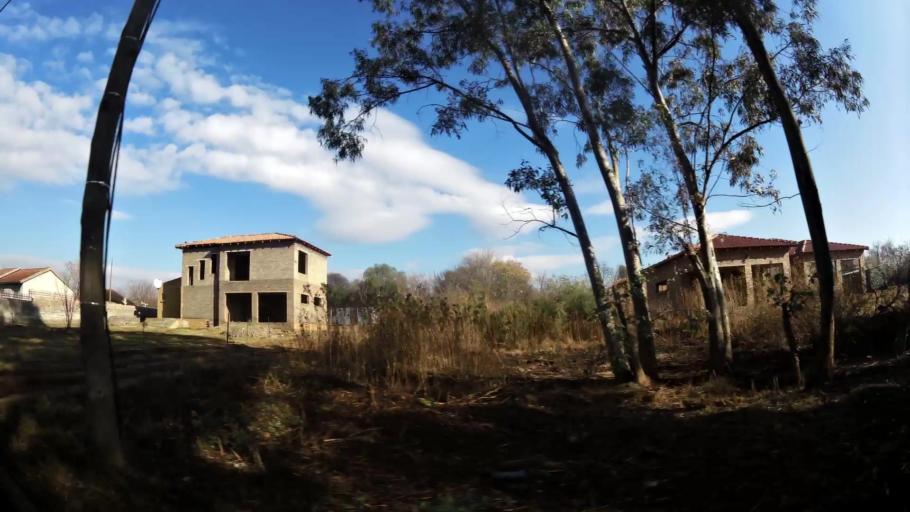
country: ZA
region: Gauteng
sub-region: Sedibeng District Municipality
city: Meyerton
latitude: -26.4961
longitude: 28.0703
